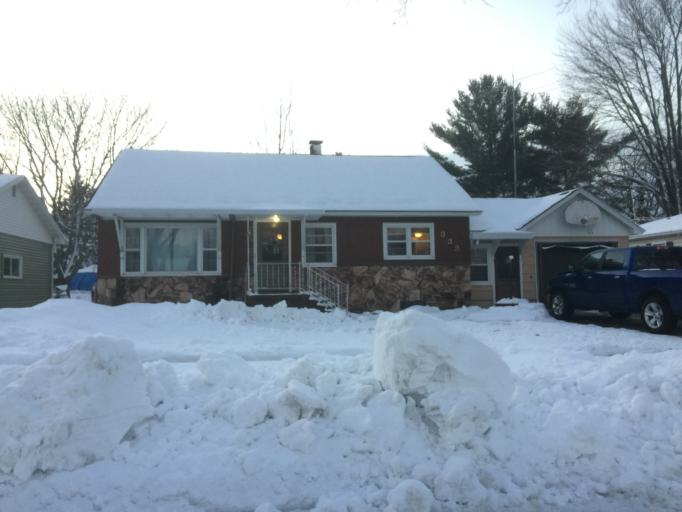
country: US
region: Wisconsin
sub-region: Marinette County
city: Peshtigo
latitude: 45.0499
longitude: -87.7565
